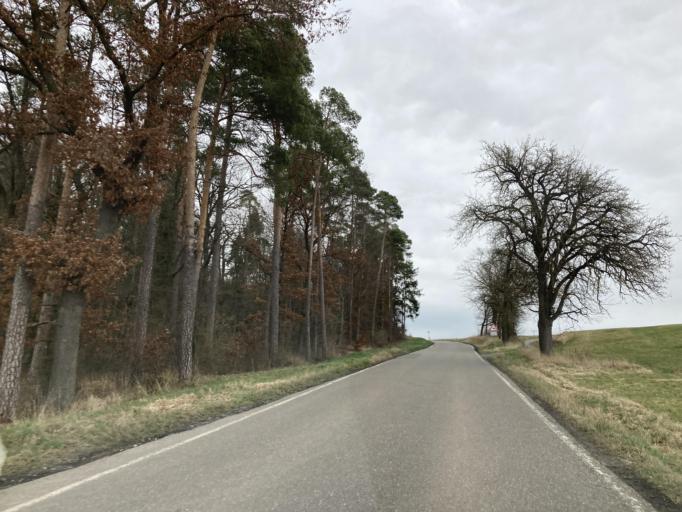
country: DE
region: Baden-Wuerttemberg
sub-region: Tuebingen Region
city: Rottenburg
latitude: 48.5039
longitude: 8.8976
